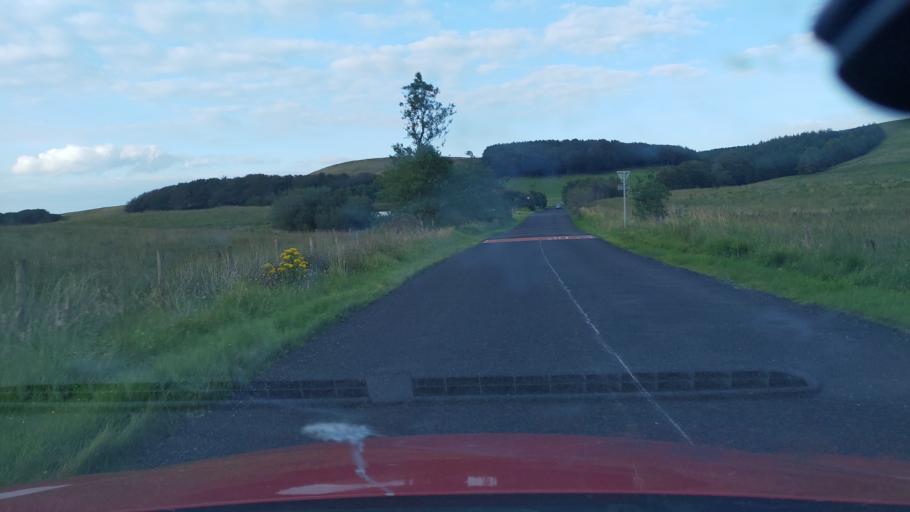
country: GB
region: England
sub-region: Blackburn with Darwen
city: Darwen
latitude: 53.6667
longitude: -2.5092
